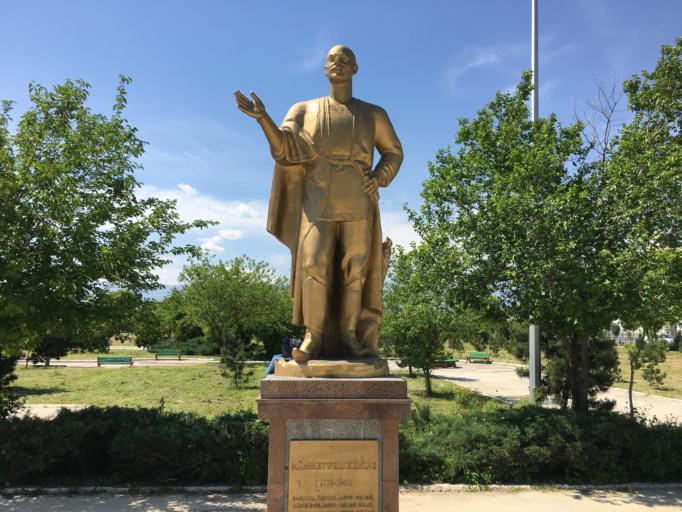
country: TM
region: Ahal
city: Ashgabat
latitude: 37.9306
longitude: 58.3938
